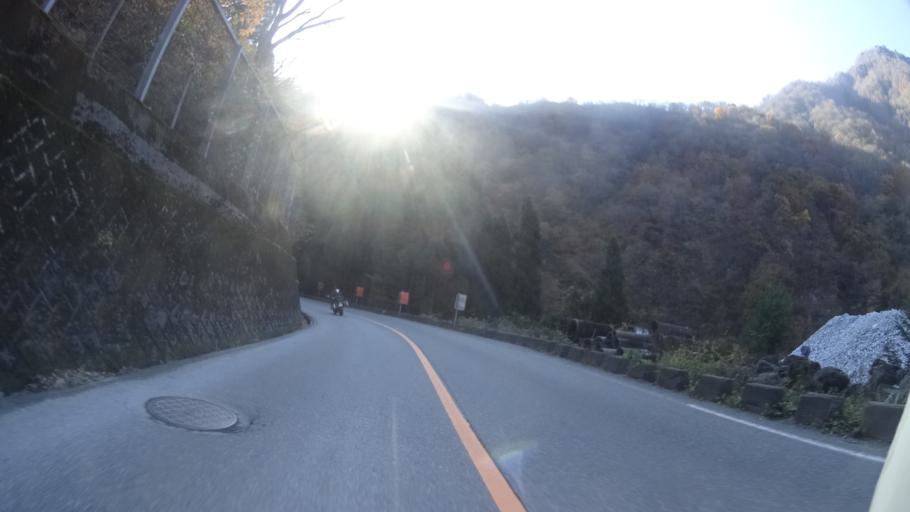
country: JP
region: Fukui
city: Ono
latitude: 35.9288
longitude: 136.6335
